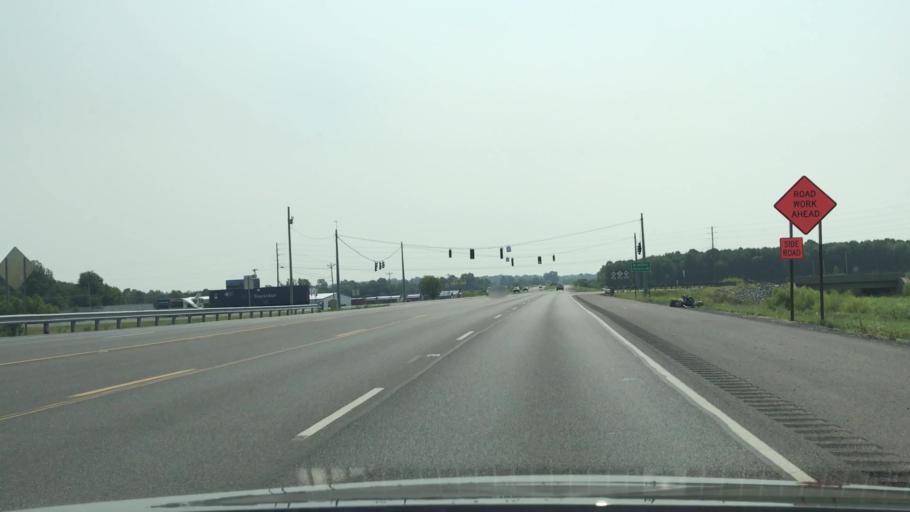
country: US
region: Kentucky
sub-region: Graves County
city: Mayfield
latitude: 36.7160
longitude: -88.6234
